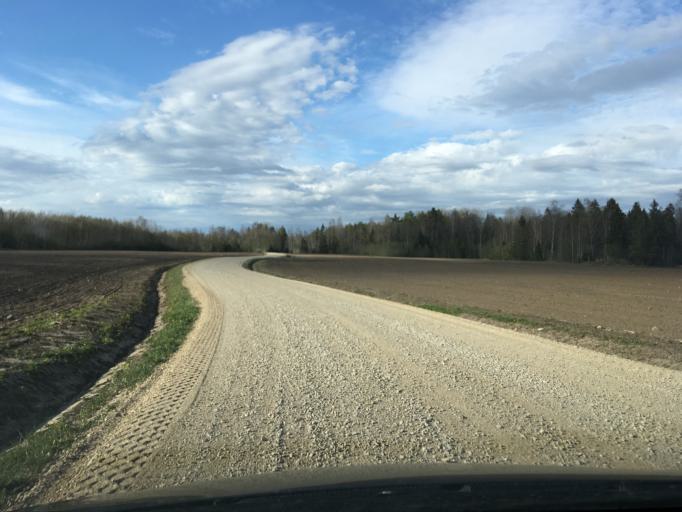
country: EE
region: Raplamaa
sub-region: Maerjamaa vald
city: Marjamaa
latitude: 58.9816
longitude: 24.3625
